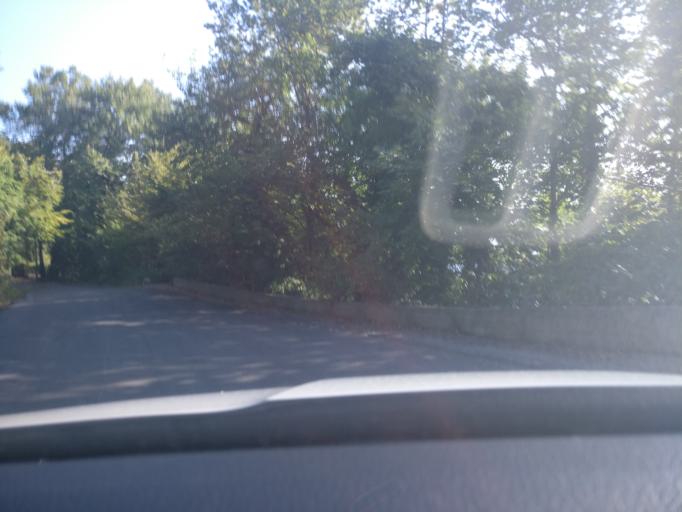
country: GR
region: Thessaly
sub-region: Nomos Magnisias
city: Zagora
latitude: 39.3799
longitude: 23.1848
